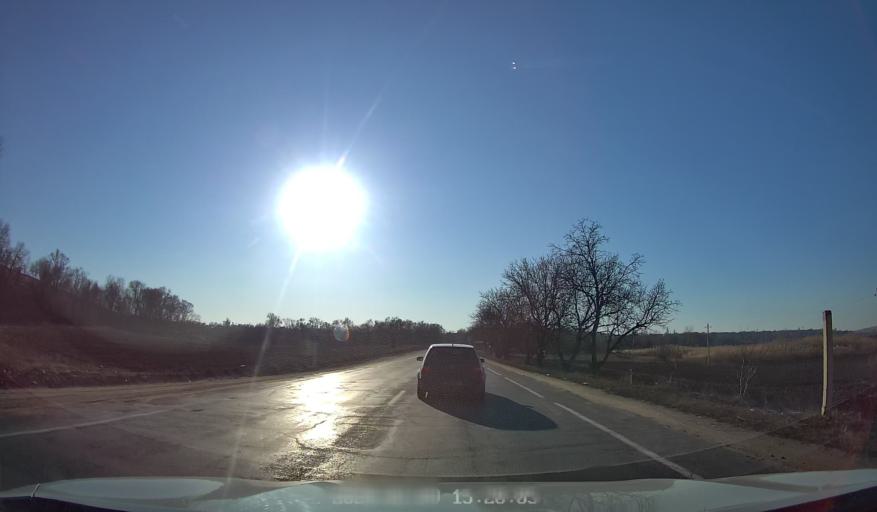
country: MD
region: Chisinau
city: Singera
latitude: 46.9178
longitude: 29.0643
